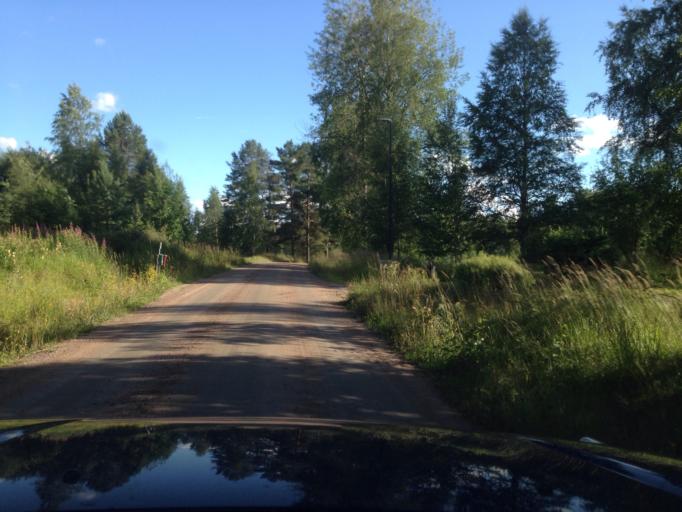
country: SE
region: Dalarna
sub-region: Ludvika Kommun
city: Abborrberget
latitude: 60.2751
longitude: 14.7285
